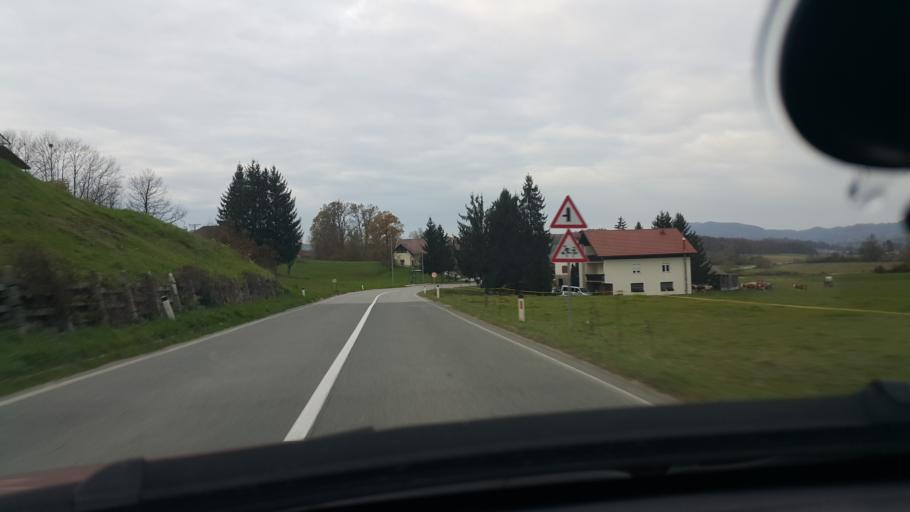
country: SI
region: Bistrica ob Sotli
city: Bistrica ob Sotli
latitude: 46.0895
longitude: 15.6198
